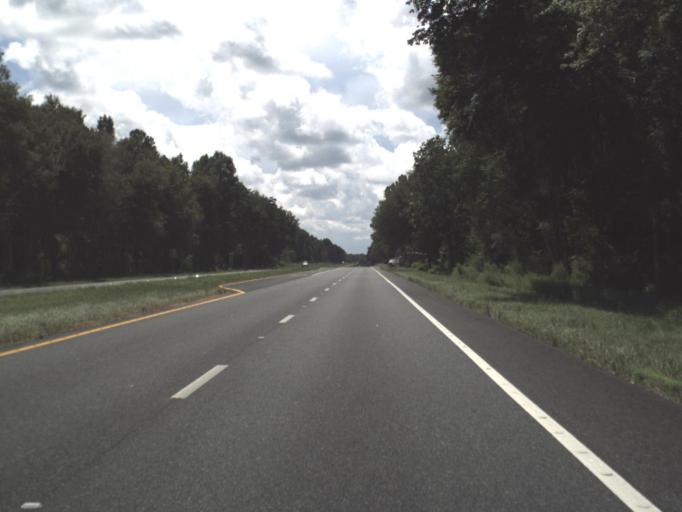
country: US
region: Florida
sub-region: Taylor County
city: Perry
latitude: 30.2037
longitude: -83.6581
